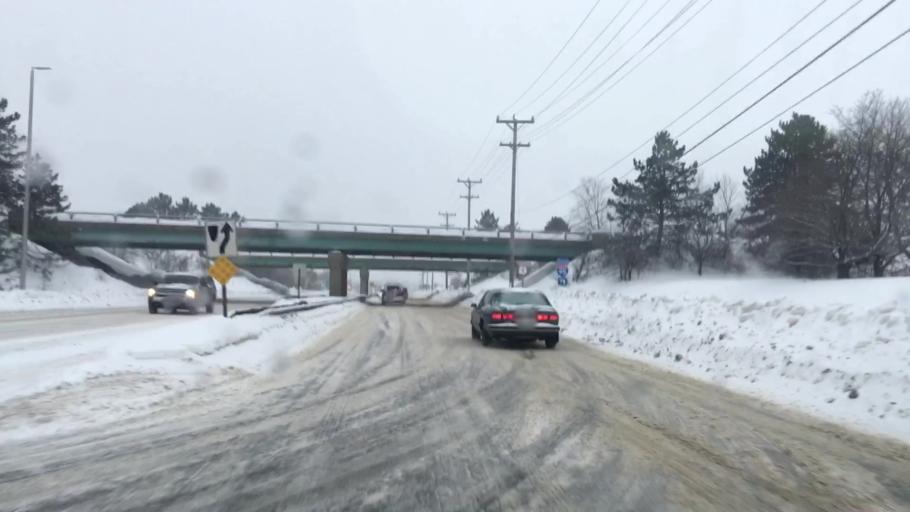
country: US
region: Maine
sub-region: Aroostook County
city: Houlton
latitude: 46.1386
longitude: -67.8397
